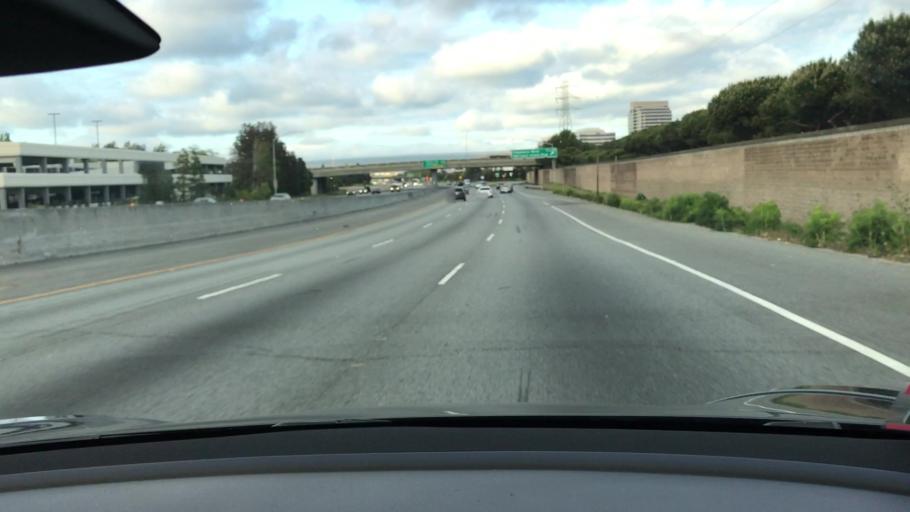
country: US
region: California
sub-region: San Mateo County
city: Foster City
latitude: 37.5552
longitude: -122.2876
